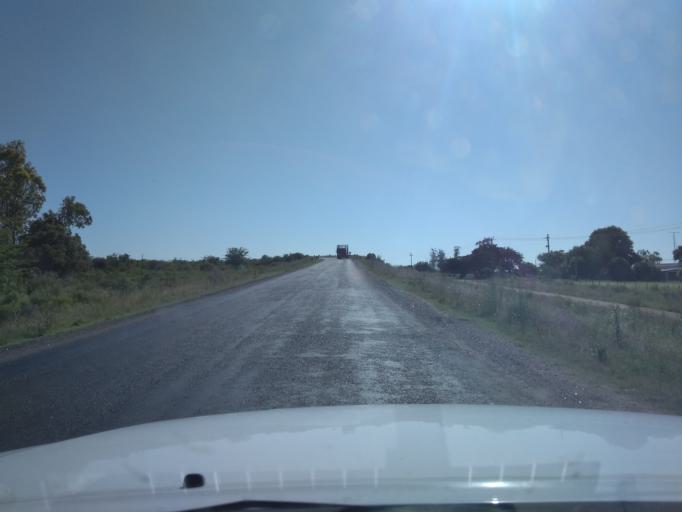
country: UY
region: Canelones
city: San Ramon
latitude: -34.2674
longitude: -55.9323
